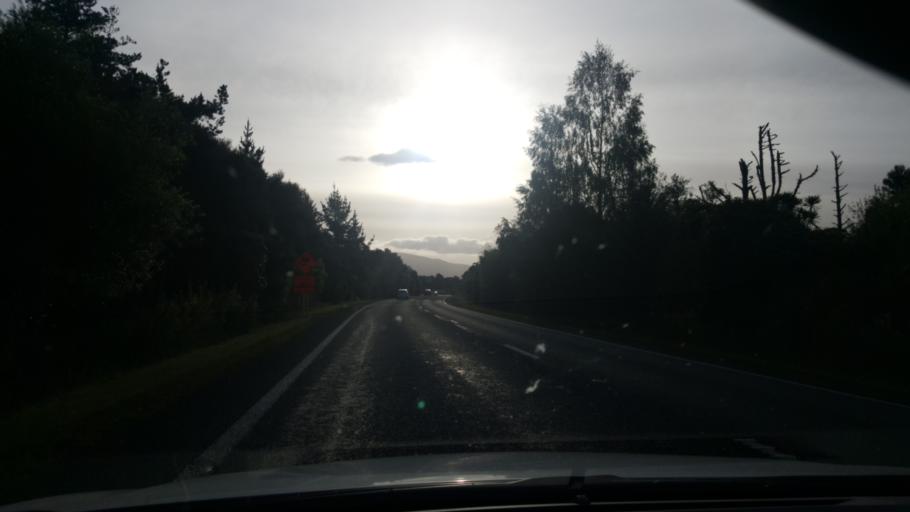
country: NZ
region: Waikato
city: Turangi
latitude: -38.9371
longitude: 175.8647
